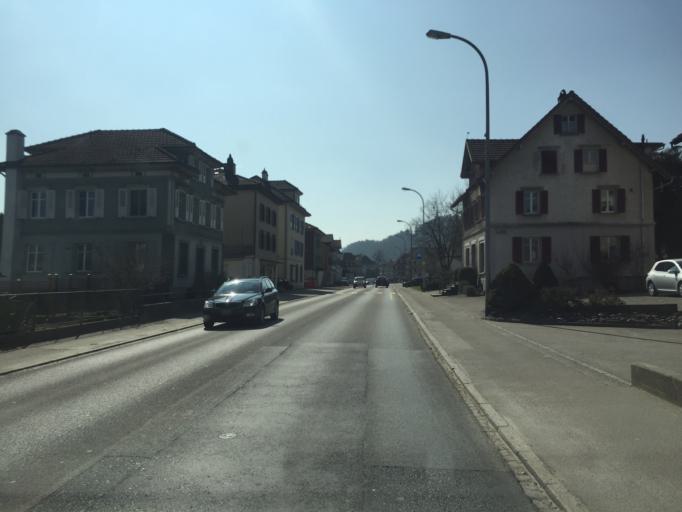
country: CH
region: Saint Gallen
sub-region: Wahlkreis Toggenburg
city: Buetschwil
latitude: 47.3610
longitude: 9.0739
